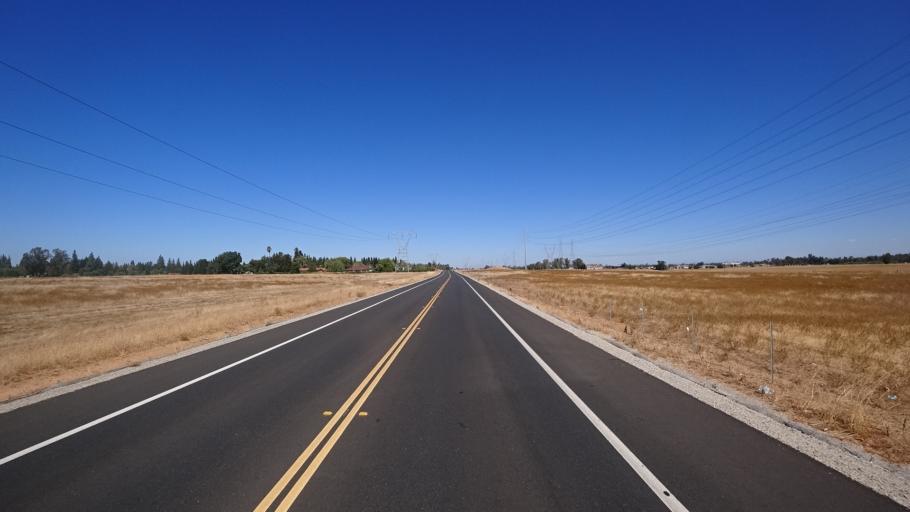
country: US
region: California
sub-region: Sacramento County
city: Elk Grove
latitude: 38.4323
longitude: -121.3532
